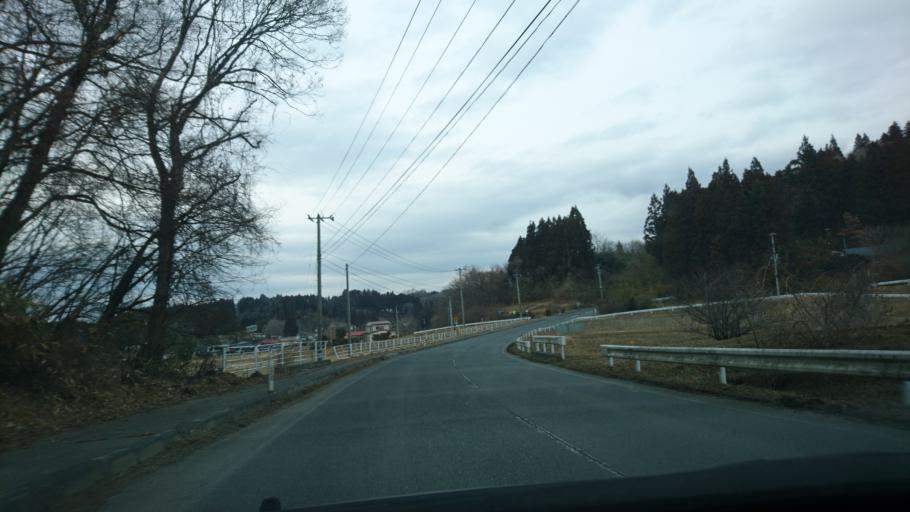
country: JP
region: Iwate
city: Ichinoseki
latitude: 38.9515
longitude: 141.3611
